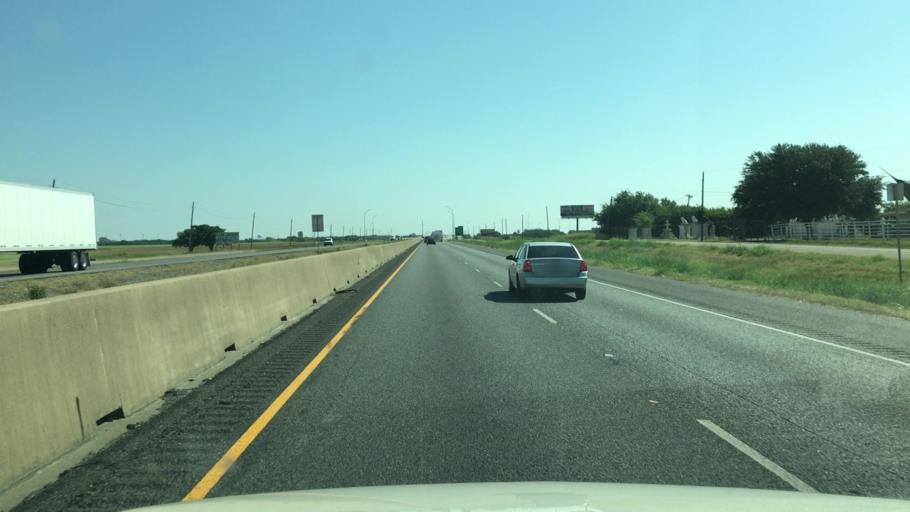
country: US
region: Texas
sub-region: Hunt County
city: Greenville
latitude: 33.0798
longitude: -96.1359
